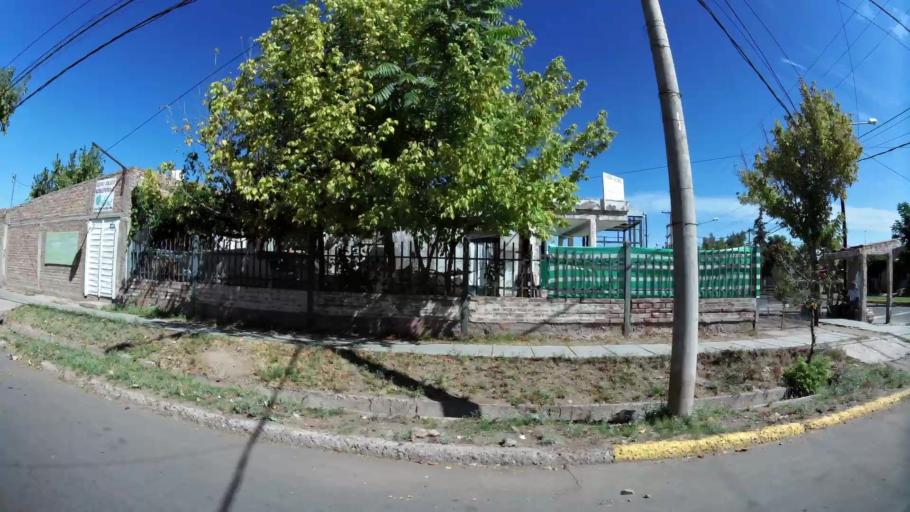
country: AR
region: Mendoza
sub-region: Departamento de Godoy Cruz
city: Godoy Cruz
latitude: -32.9571
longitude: -68.8313
